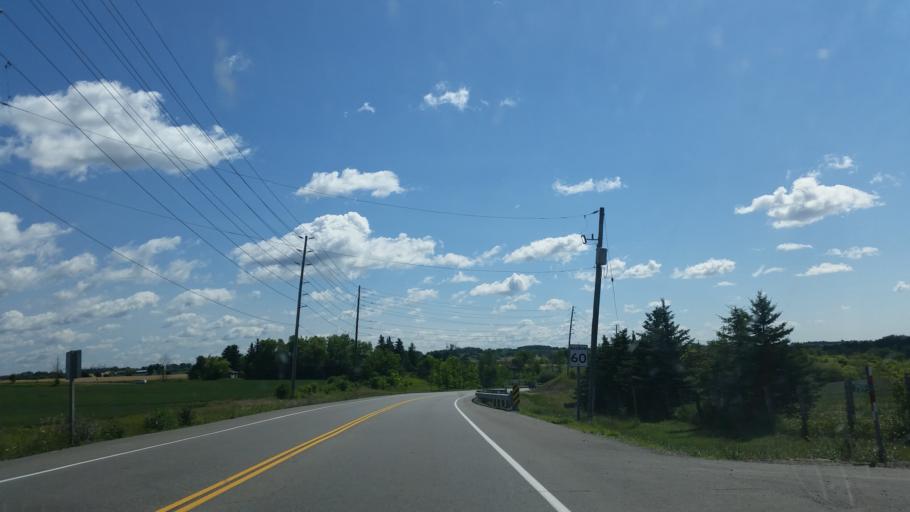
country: CA
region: Ontario
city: Vaughan
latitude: 43.8909
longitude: -79.7049
